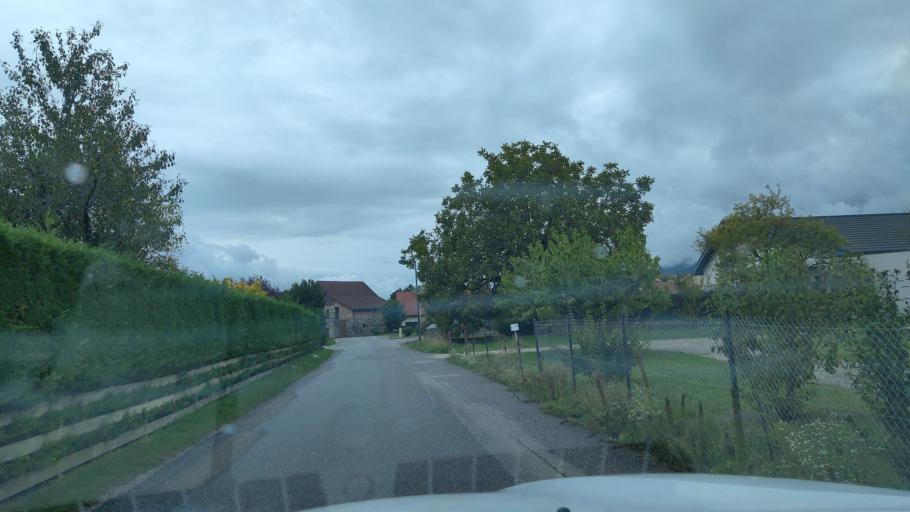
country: FR
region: Rhone-Alpes
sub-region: Departement de la Savoie
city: Les Marches
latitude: 45.5071
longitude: 5.9997
